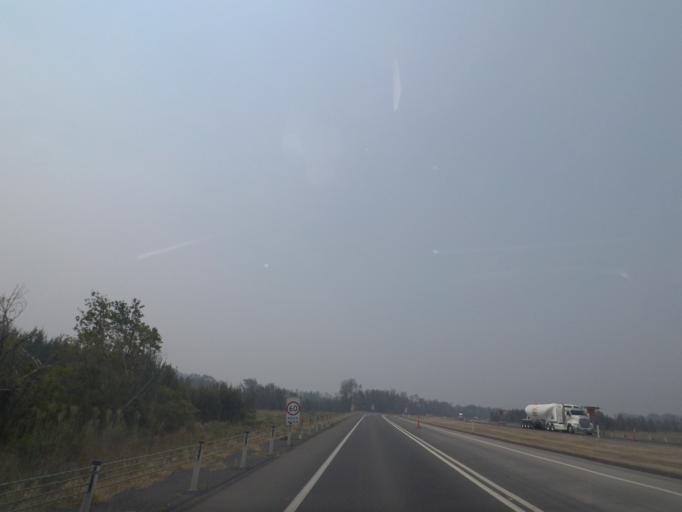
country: AU
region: New South Wales
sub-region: Ballina
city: Ballina
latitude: -28.8712
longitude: 153.4908
